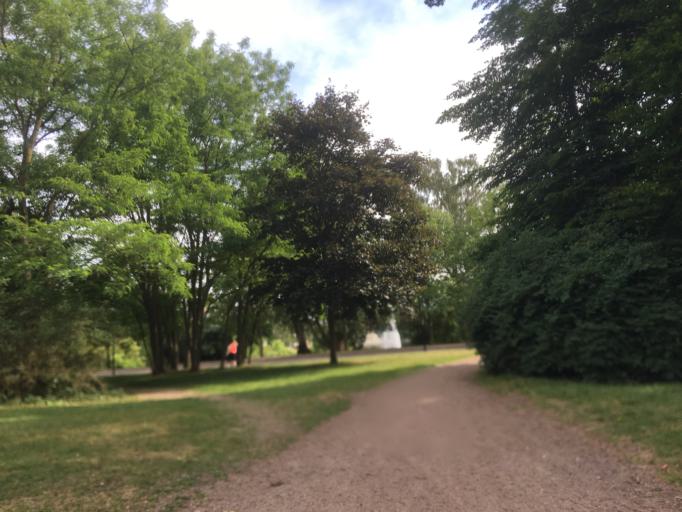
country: SE
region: Skane
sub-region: Landskrona
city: Landskrona
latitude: 55.8764
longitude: 12.8425
